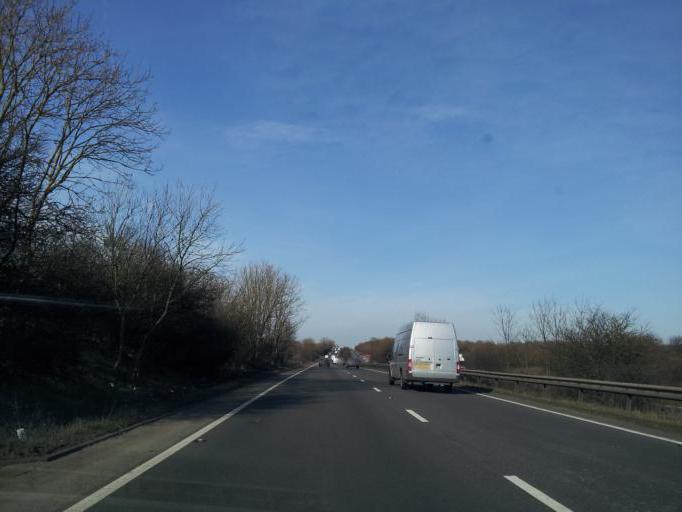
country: GB
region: England
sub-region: District of Rutland
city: Clipsham
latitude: 52.7116
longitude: -0.5922
